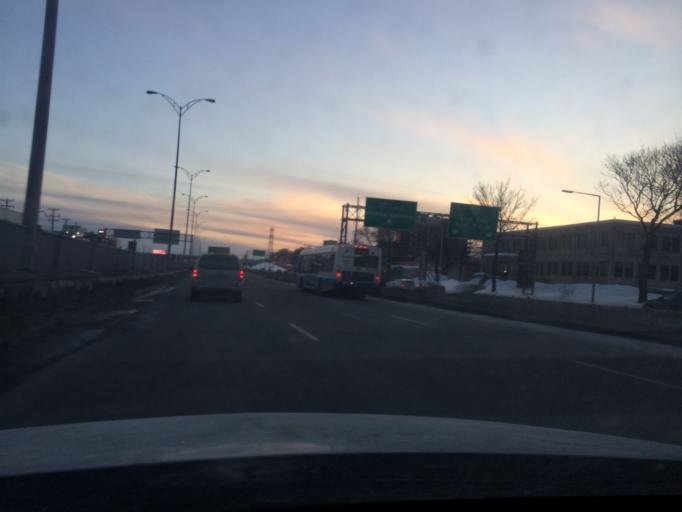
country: CA
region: Quebec
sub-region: Montreal
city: Saint-Leonard
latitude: 45.5799
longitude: -73.5911
